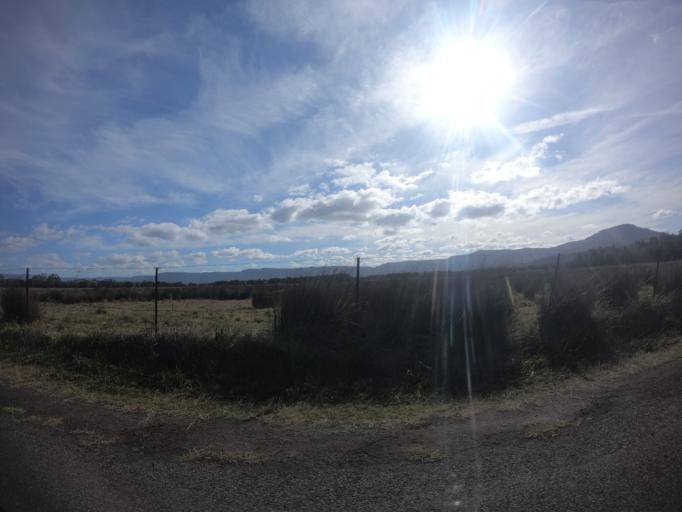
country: AU
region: New South Wales
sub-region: Wollongong
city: Berkeley
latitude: -34.4807
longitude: 150.8334
